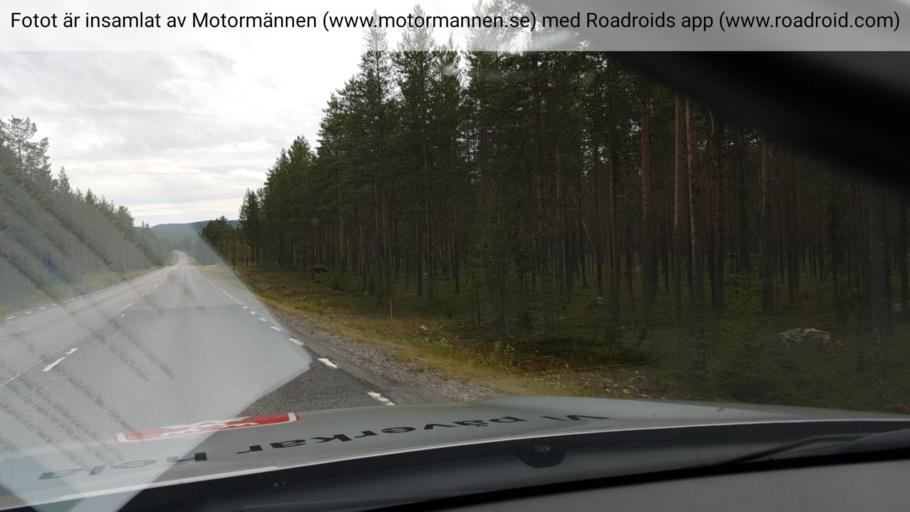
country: SE
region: Norrbotten
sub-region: Overkalix Kommun
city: OEverkalix
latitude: 66.2356
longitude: 22.7997
